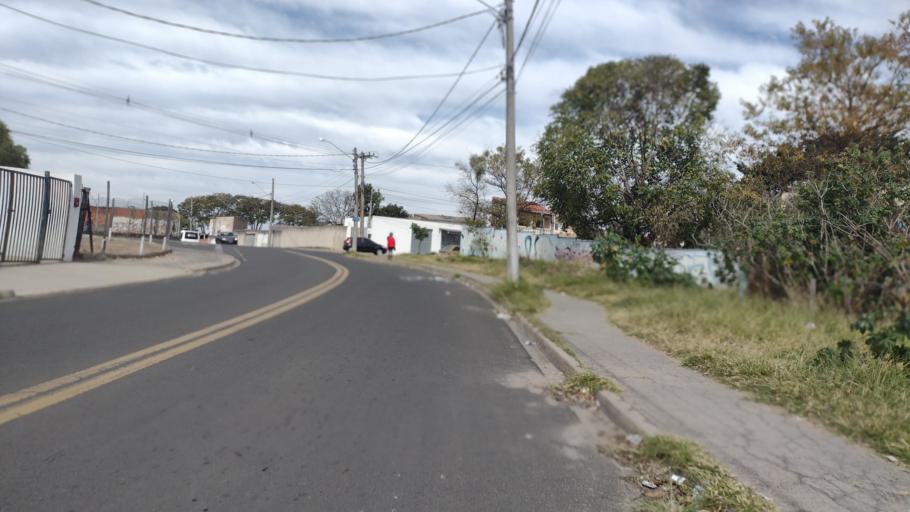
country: BR
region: Sao Paulo
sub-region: Sorocaba
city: Sorocaba
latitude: -23.4277
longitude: -47.4607
